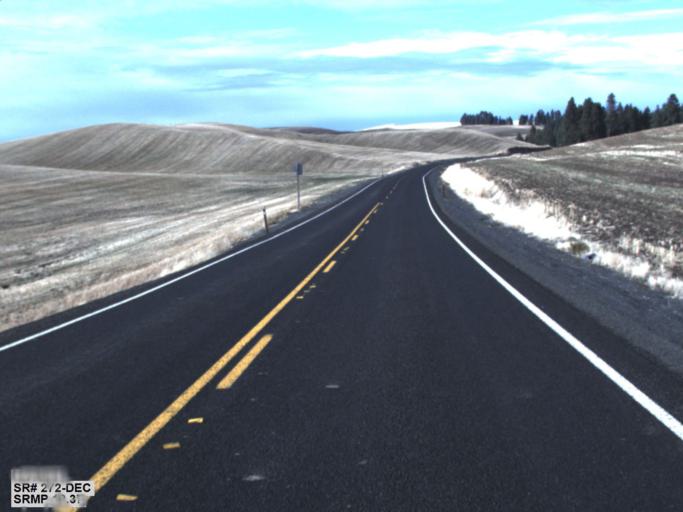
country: US
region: Washington
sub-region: Whitman County
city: Pullman
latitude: 46.9351
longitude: -117.1419
